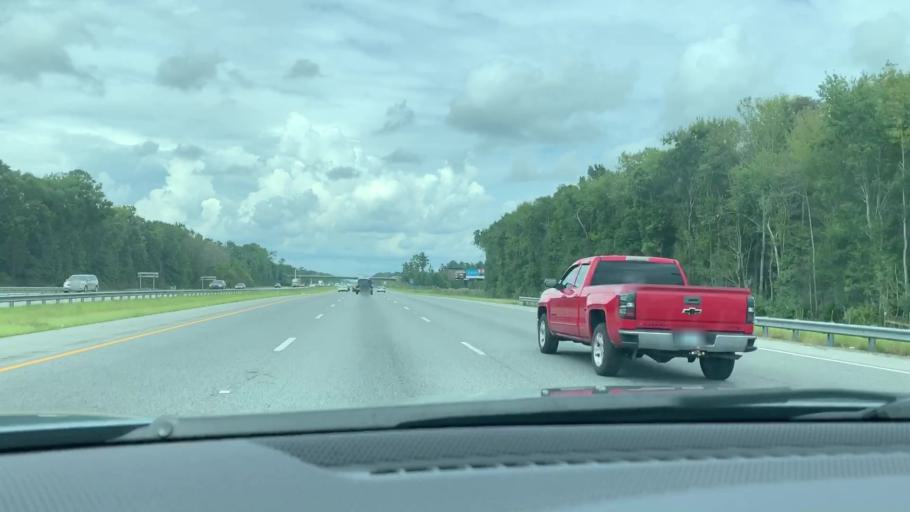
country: US
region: Georgia
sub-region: McIntosh County
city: Darien
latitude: 31.4875
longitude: -81.4469
